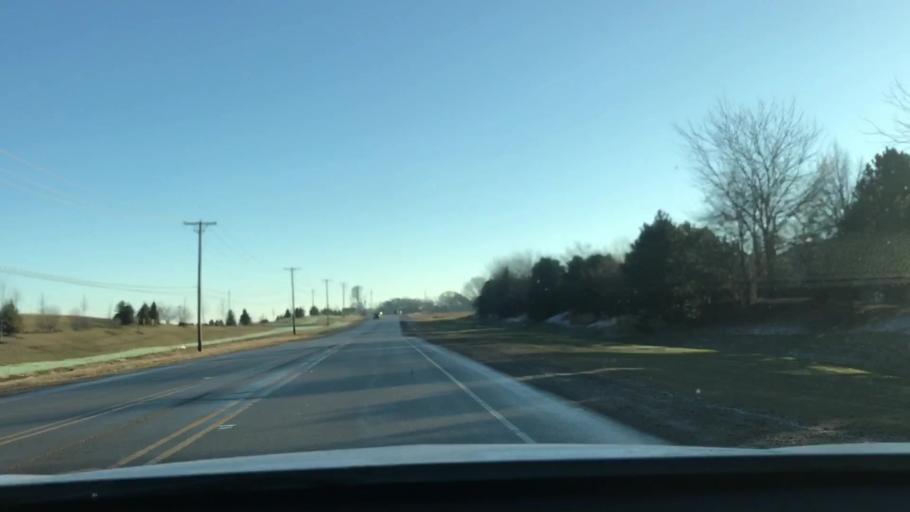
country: US
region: Illinois
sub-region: Kane County
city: Pingree Grove
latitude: 42.0886
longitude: -88.4351
